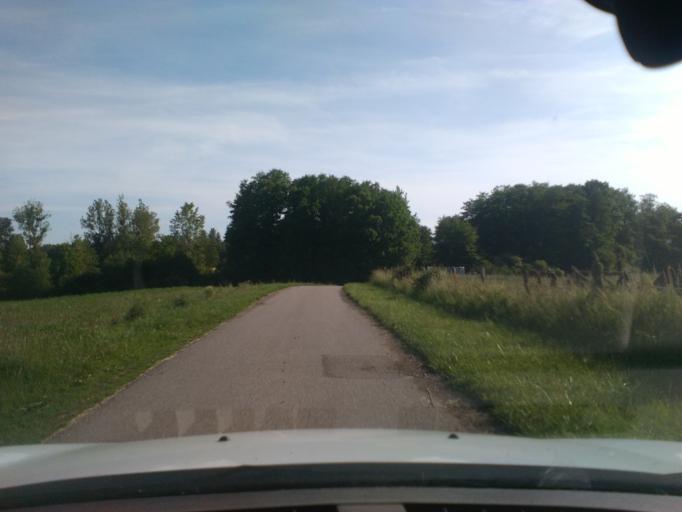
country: FR
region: Lorraine
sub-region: Departement des Vosges
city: Mirecourt
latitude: 48.2646
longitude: 6.2102
